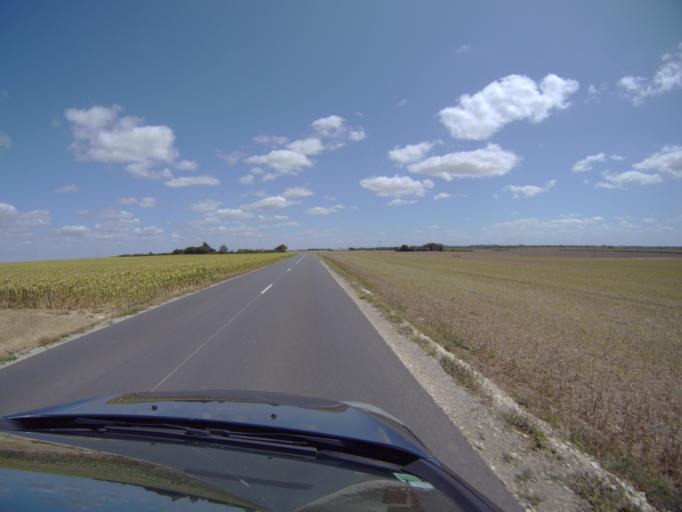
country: FR
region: Poitou-Charentes
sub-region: Departement de la Charente-Maritime
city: Marans
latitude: 46.2862
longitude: -0.9379
